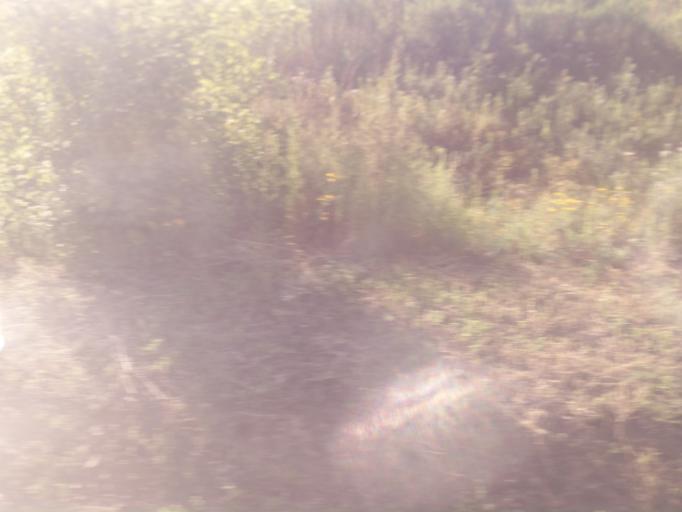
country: RU
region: Rostov
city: Krasnyy Sulin
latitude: 47.8753
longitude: 40.1239
